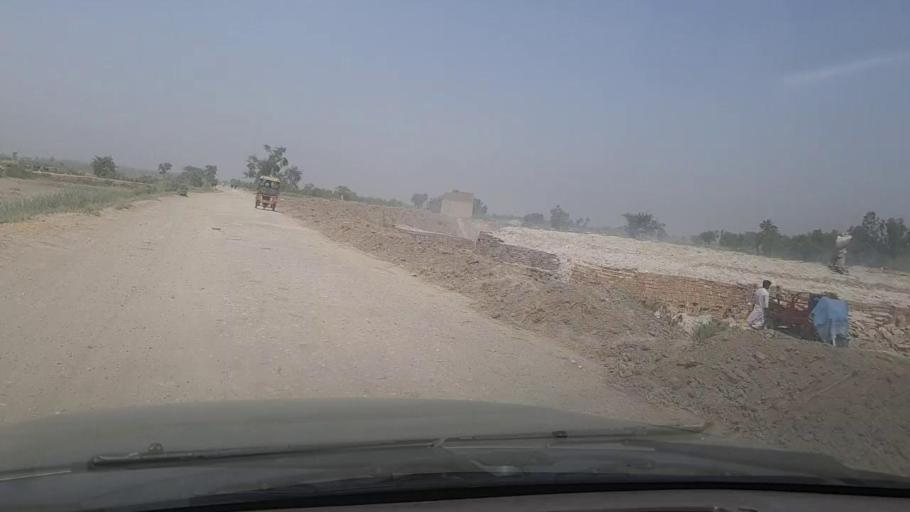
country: PK
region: Sindh
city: Madeji
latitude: 27.7969
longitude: 68.4473
